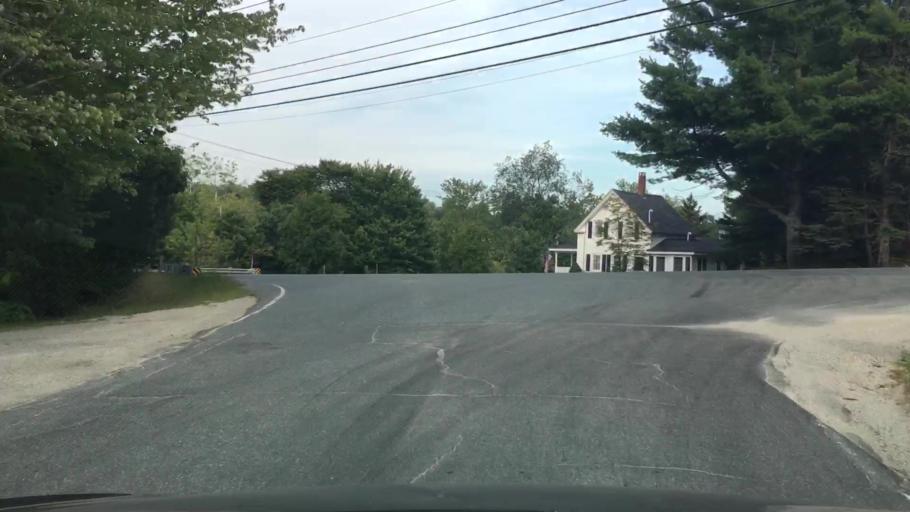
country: US
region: Maine
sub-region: Hancock County
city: Surry
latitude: 44.4943
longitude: -68.5071
